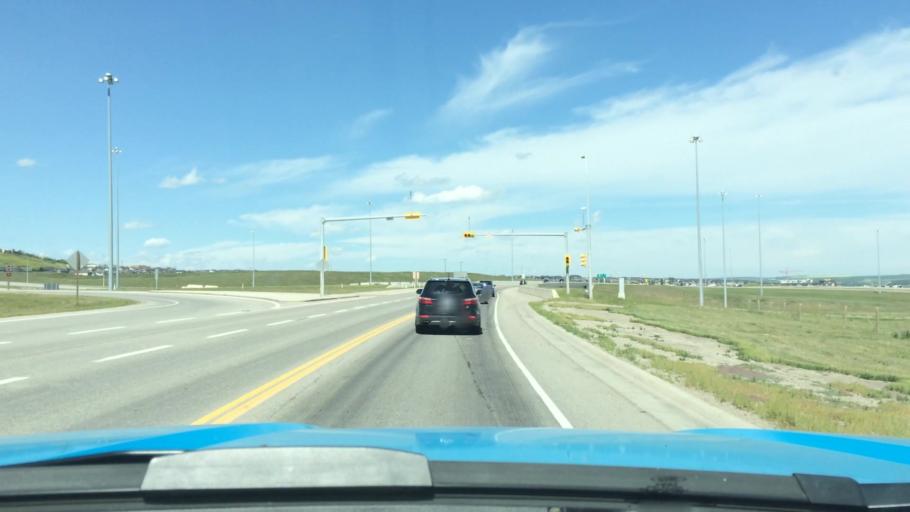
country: CA
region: Alberta
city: Calgary
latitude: 51.1399
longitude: -114.1470
